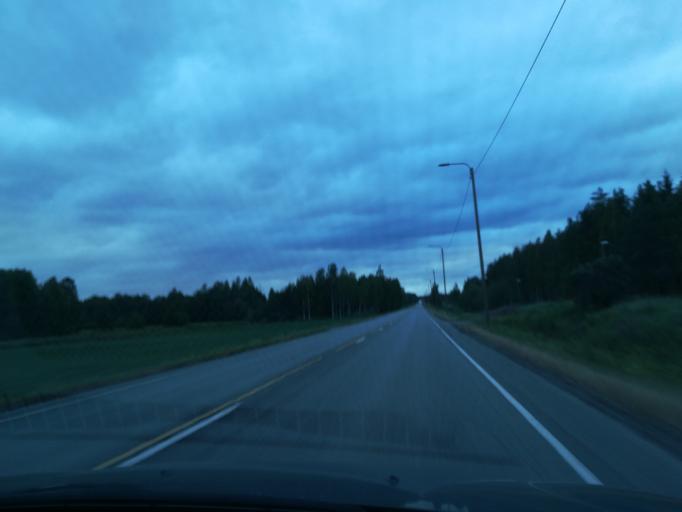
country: FI
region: Southern Savonia
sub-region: Mikkeli
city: Ristiina
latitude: 61.4838
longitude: 27.2494
